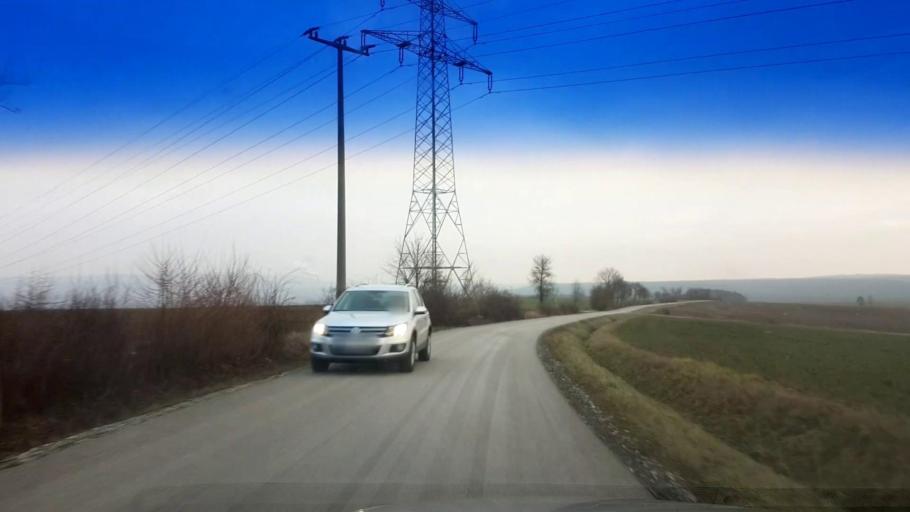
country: DE
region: Bavaria
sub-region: Upper Franconia
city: Hallerndorf
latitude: 49.7783
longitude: 10.9825
